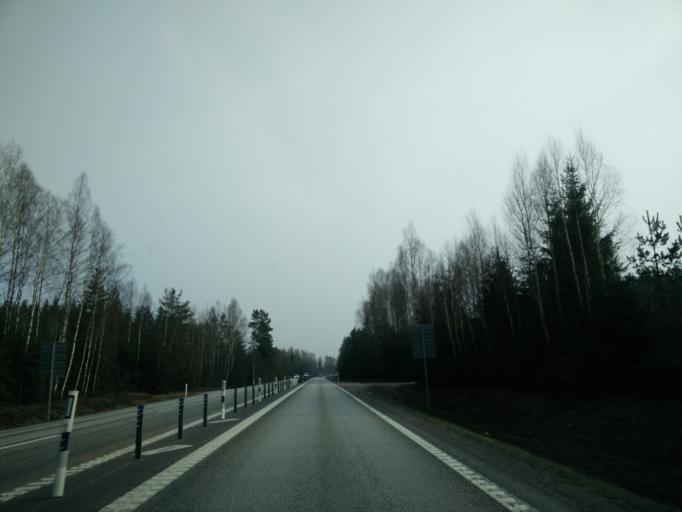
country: SE
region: Vaermland
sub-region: Forshaga Kommun
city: Forshaga
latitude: 59.4684
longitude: 13.4134
